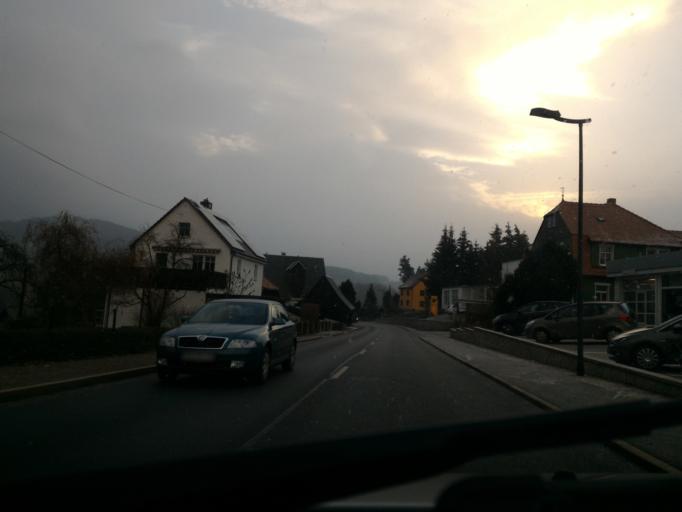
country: DE
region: Saxony
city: Grossschonau
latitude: 50.8928
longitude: 14.6790
